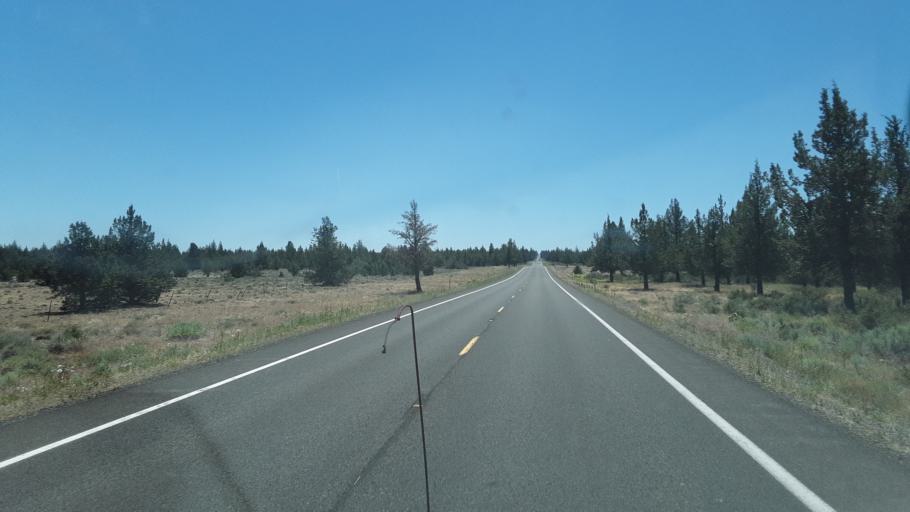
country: US
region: California
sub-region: Siskiyou County
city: Tulelake
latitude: 41.6474
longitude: -121.2397
